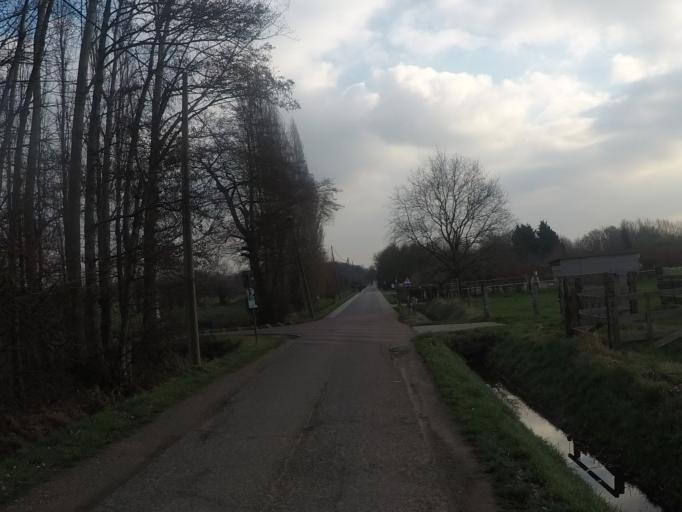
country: BE
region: Flanders
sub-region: Provincie Antwerpen
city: Stabroek
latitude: 51.3209
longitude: 4.4014
